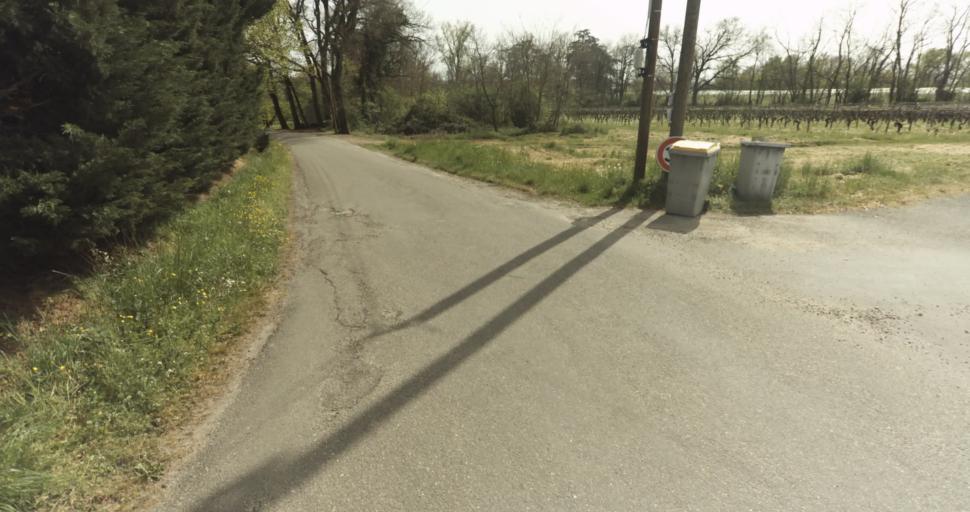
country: FR
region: Midi-Pyrenees
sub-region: Departement du Tarn-et-Garonne
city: Moissac
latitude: 44.1247
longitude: 1.1452
